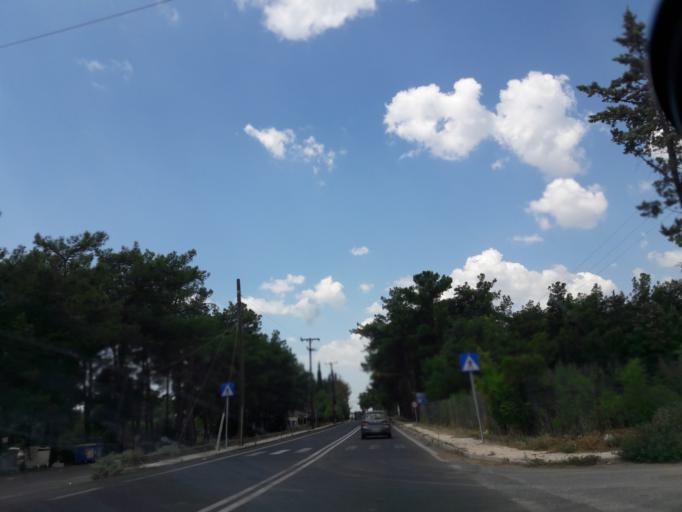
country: GR
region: Central Macedonia
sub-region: Nomos Thessalonikis
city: Souroti
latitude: 40.5121
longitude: 23.0783
